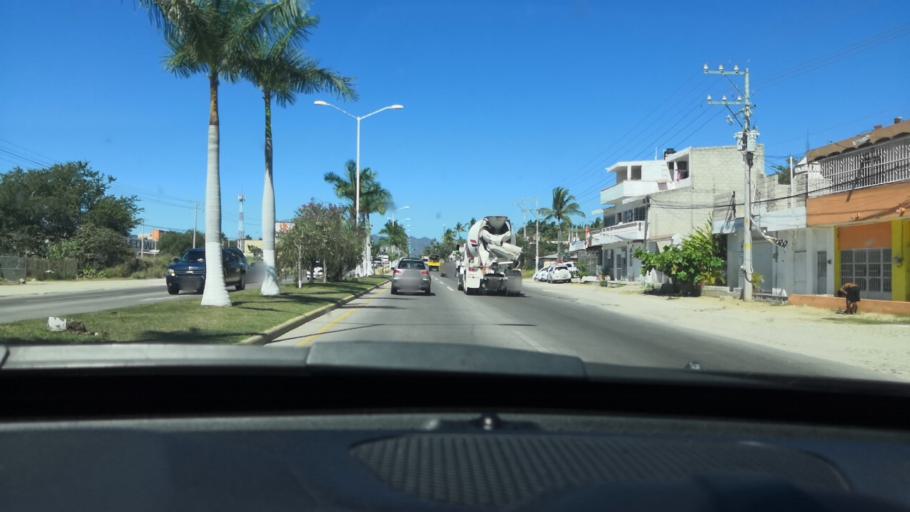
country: MX
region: Nayarit
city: Bucerias
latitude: 20.7504
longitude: -105.3221
